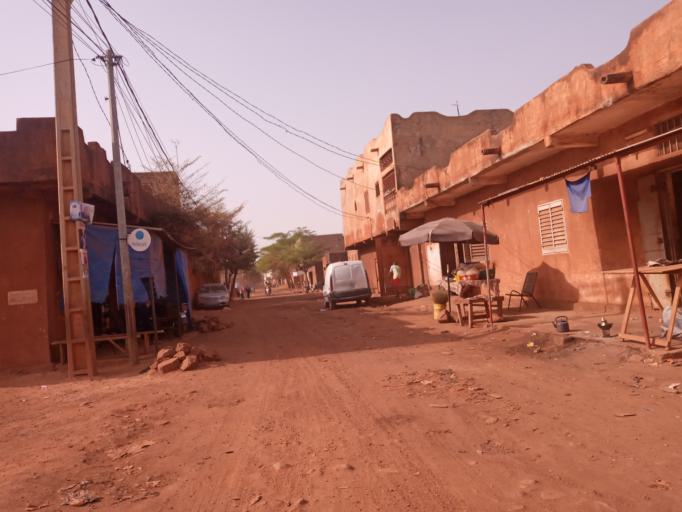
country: ML
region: Bamako
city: Bamako
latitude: 12.6810
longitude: -7.9406
